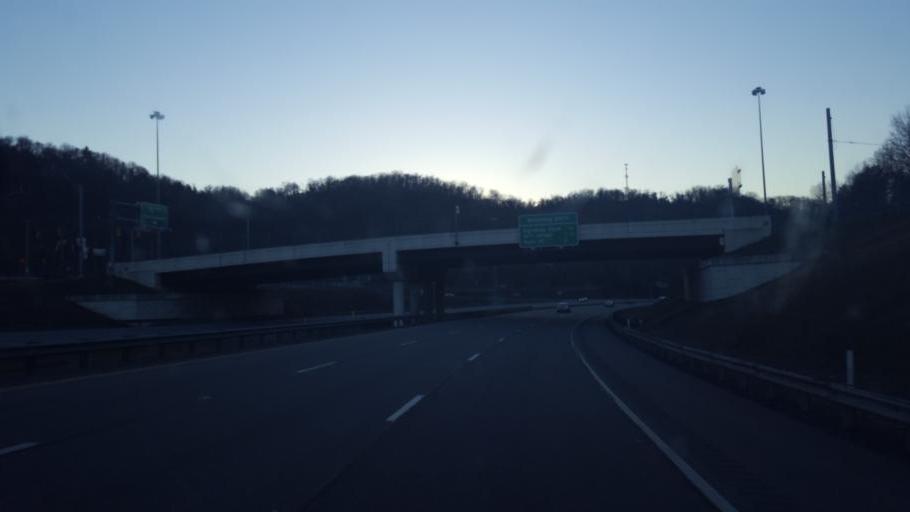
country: US
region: West Virginia
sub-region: Ohio County
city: Bethlehem
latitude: 40.0669
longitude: -80.6920
